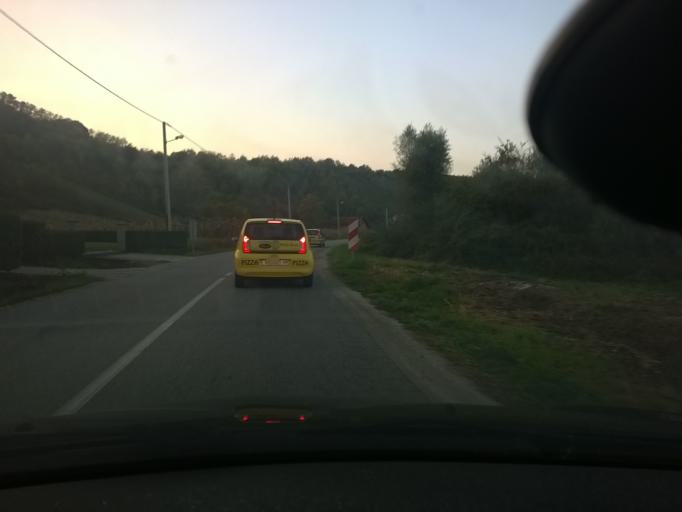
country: HR
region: Krapinsko-Zagorska
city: Zabok
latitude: 46.0623
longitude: 15.9081
